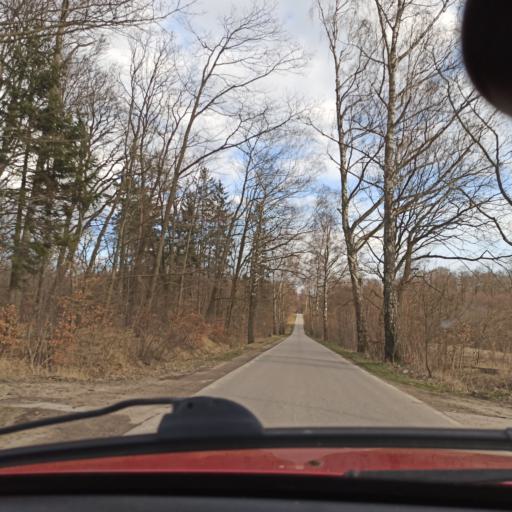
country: PL
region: Warmian-Masurian Voivodeship
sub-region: Powiat elblaski
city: Tolkmicko
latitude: 54.2615
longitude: 19.4963
